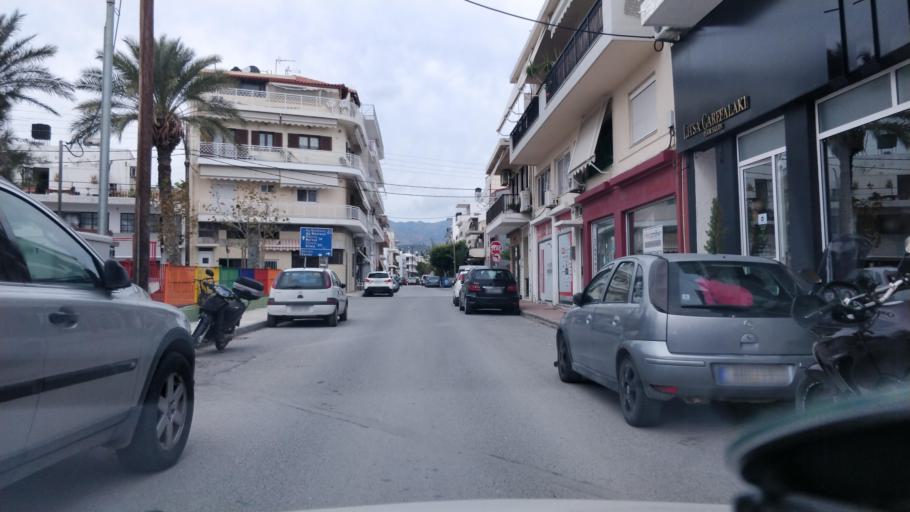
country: GR
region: Crete
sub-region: Nomos Lasithiou
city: Ierapetra
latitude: 35.0069
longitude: 25.7352
